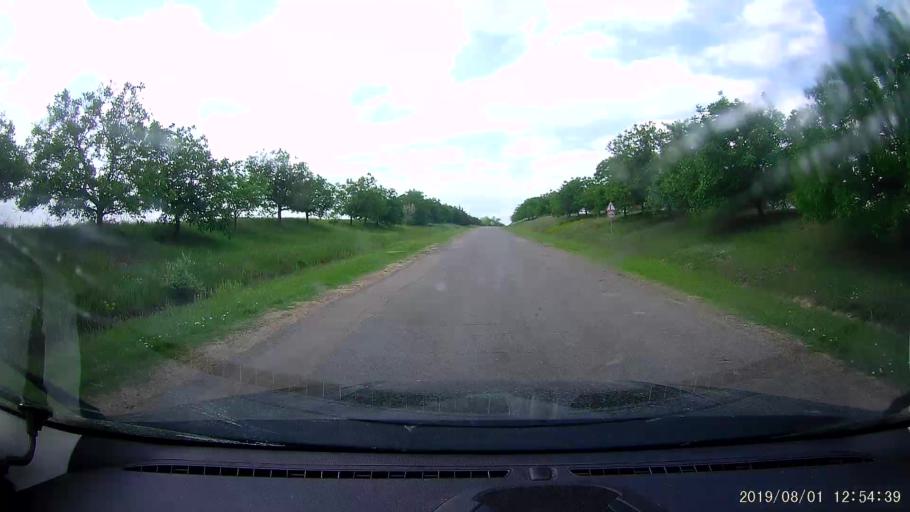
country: MD
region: Gagauzia
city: Vulcanesti
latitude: 45.6953
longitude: 28.4834
